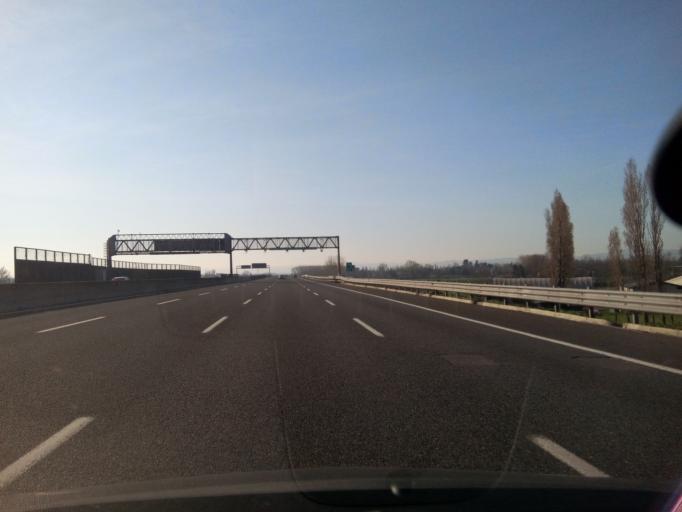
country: IT
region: Emilia-Romagna
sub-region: Provincia di Modena
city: Baggiovara
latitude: 44.6468
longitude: 10.8671
